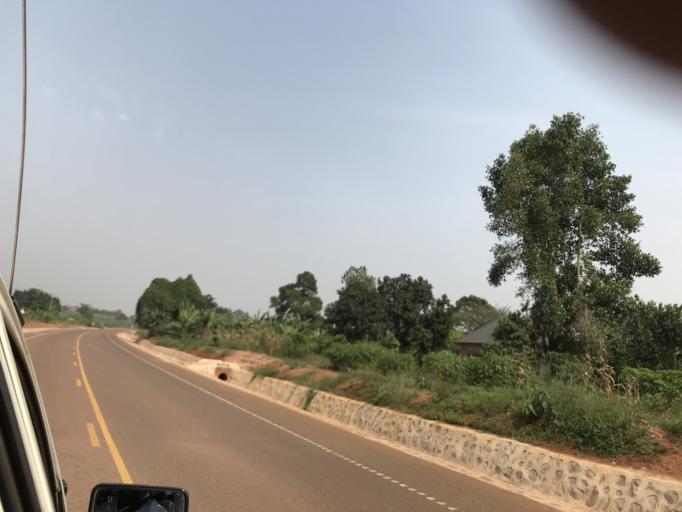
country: UG
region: Central Region
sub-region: Kalungu District
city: Kalungu
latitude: -0.2278
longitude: 31.7254
